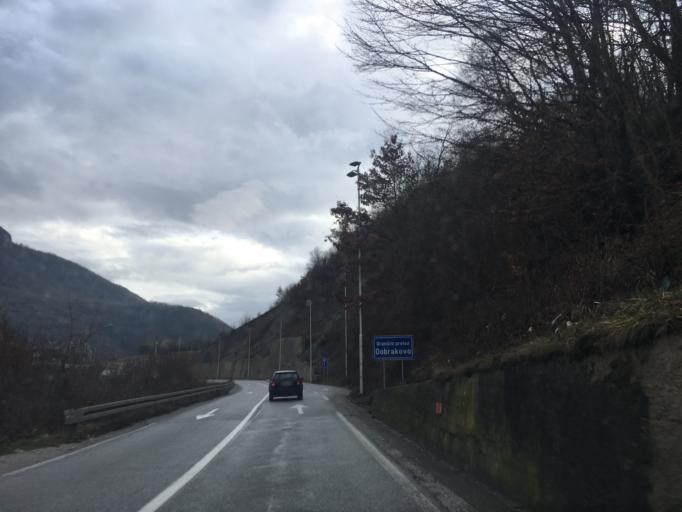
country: RS
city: Sokolovo Brdo
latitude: 43.1471
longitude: 19.7786
